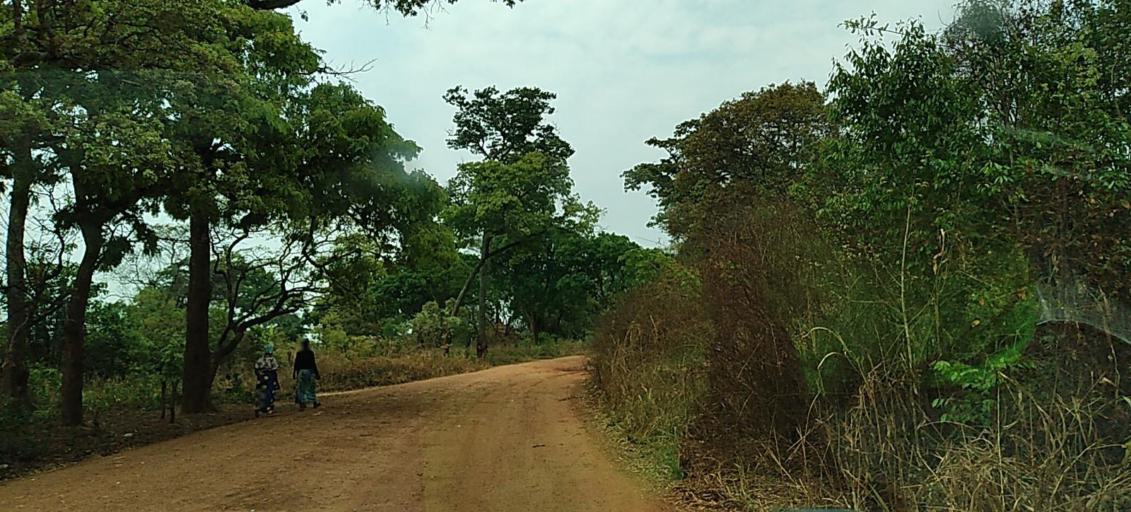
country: ZM
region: North-Western
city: Solwezi
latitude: -12.3479
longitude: 26.5300
